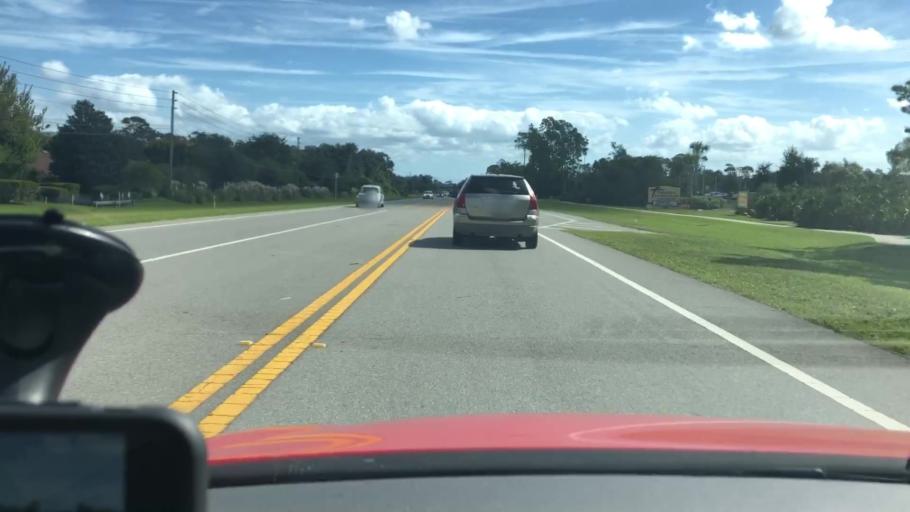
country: US
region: Florida
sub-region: Volusia County
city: Ormond Beach
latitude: 29.2617
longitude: -81.0897
